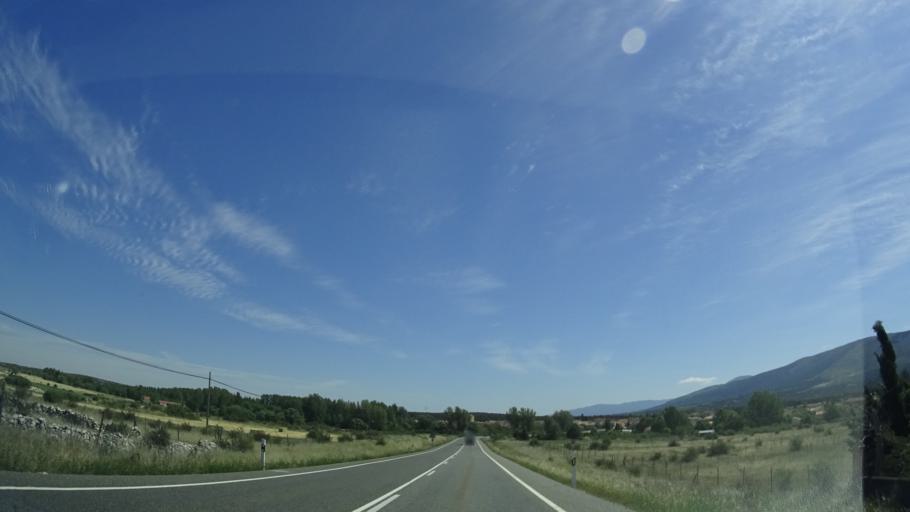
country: ES
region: Castille and Leon
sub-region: Provincia de Segovia
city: Arcones
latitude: 41.1149
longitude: -3.7288
